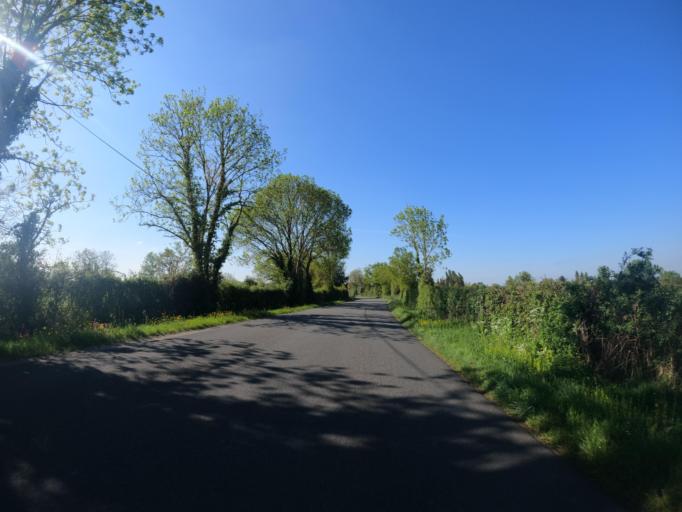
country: FR
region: Poitou-Charentes
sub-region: Departement des Deux-Sevres
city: La Chapelle-Saint-Laurent
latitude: 46.6969
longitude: -0.5171
